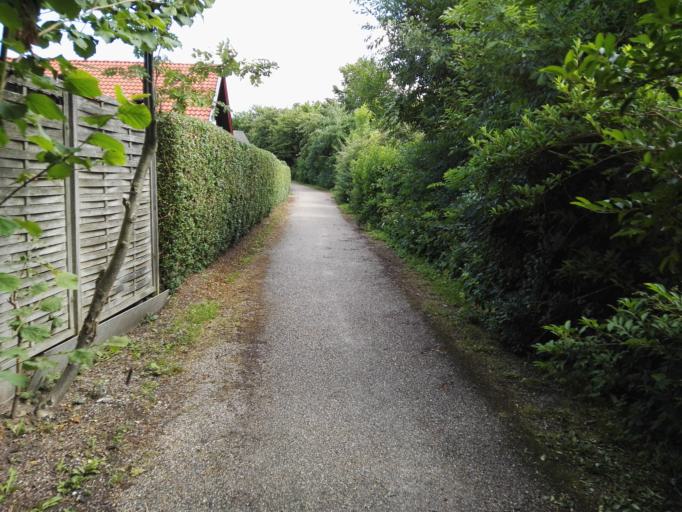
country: DK
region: Capital Region
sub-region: Herlev Kommune
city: Herlev
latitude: 55.7359
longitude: 12.4093
